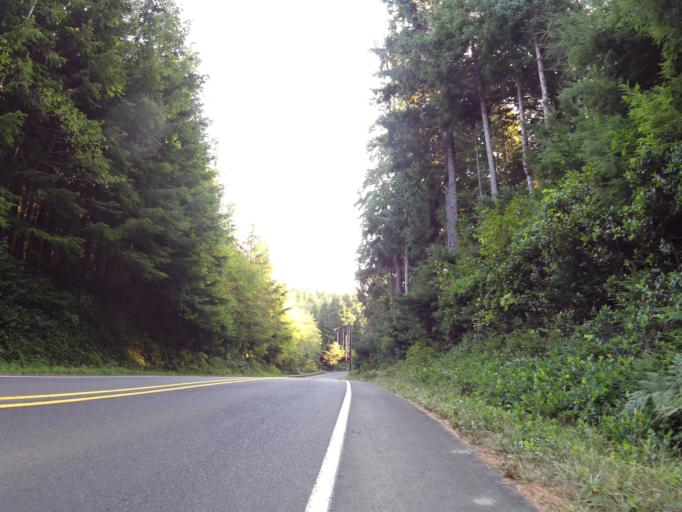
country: US
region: Oregon
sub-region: Lincoln County
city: Lincoln City
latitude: 44.9666
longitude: -123.9938
